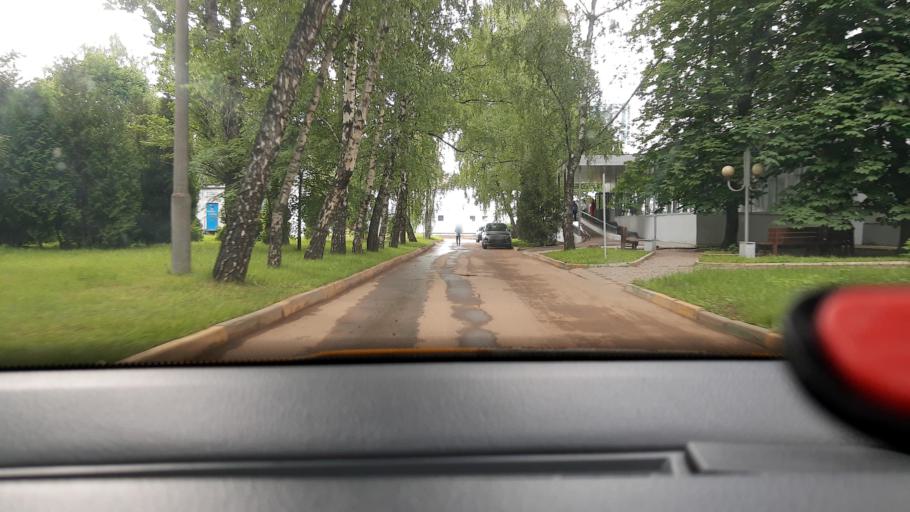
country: RU
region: Moscow
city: Lefortovo
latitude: 55.7708
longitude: 37.7386
